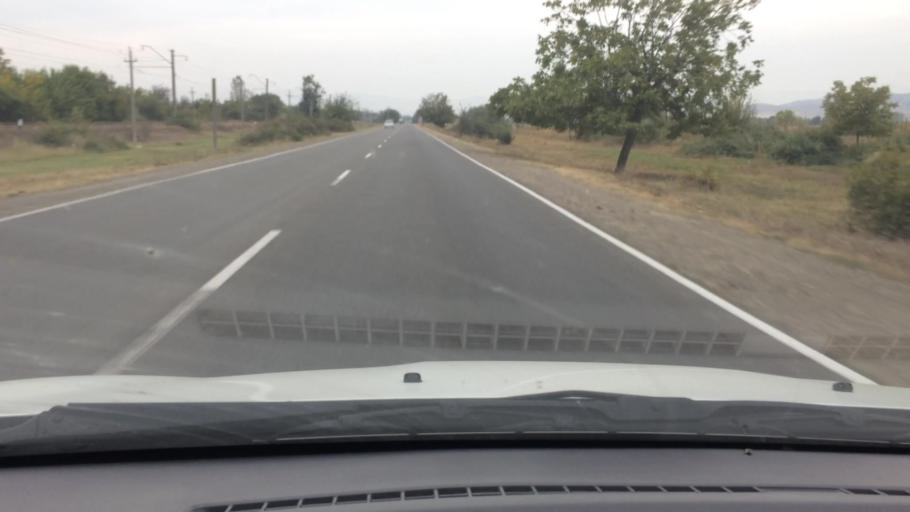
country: GE
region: Kvemo Kartli
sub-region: Marneuli
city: Marneuli
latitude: 41.4333
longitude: 44.8202
